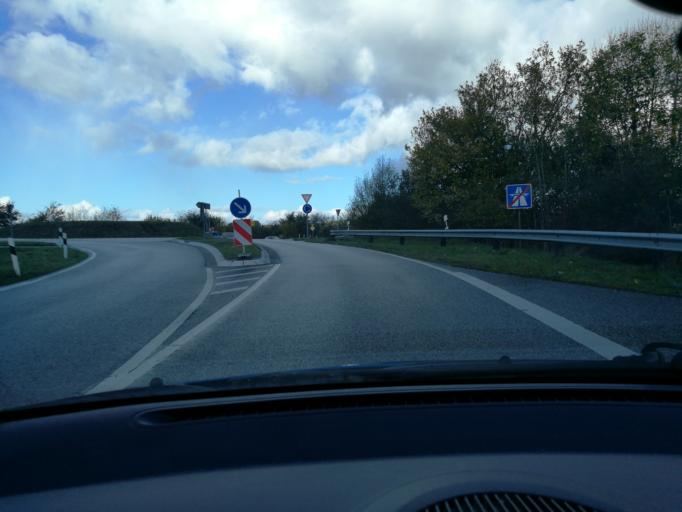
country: DE
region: Schleswig-Holstein
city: Borgstedt
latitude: 54.3476
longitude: 9.7019
